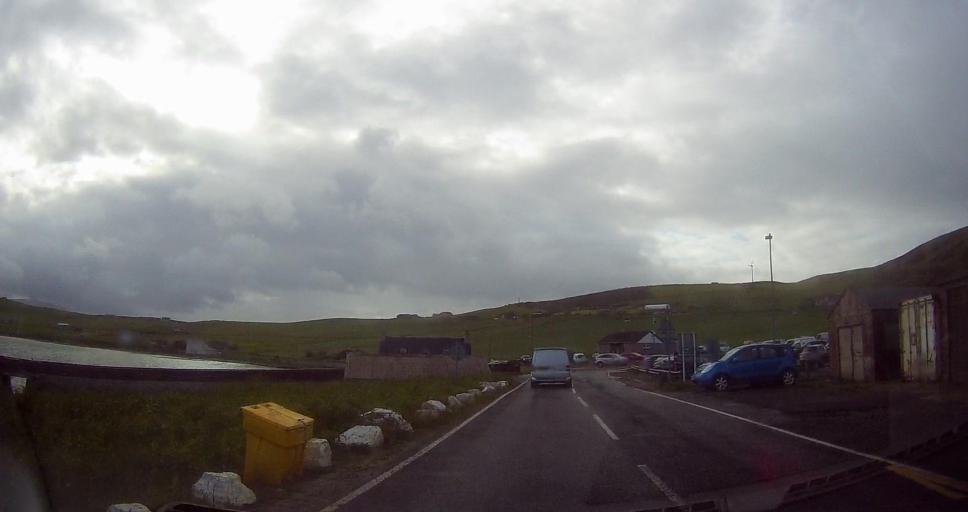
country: GB
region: Scotland
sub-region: Orkney Islands
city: Stromness
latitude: 58.9180
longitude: -3.1839
